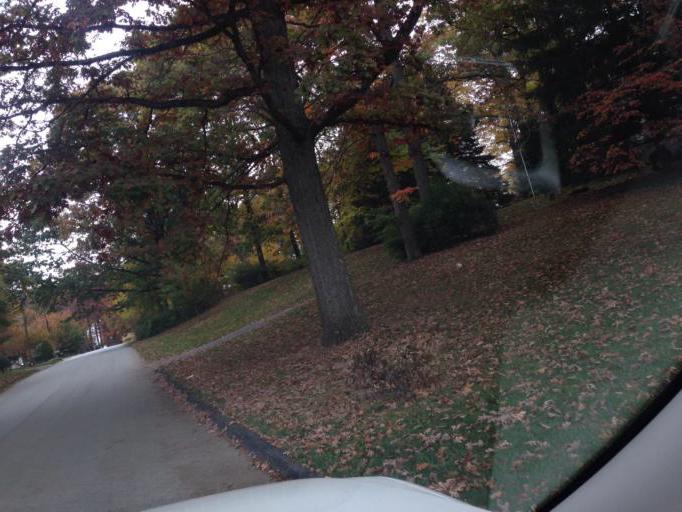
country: US
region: Maryland
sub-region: Howard County
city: Highland
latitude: 39.2625
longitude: -76.9730
